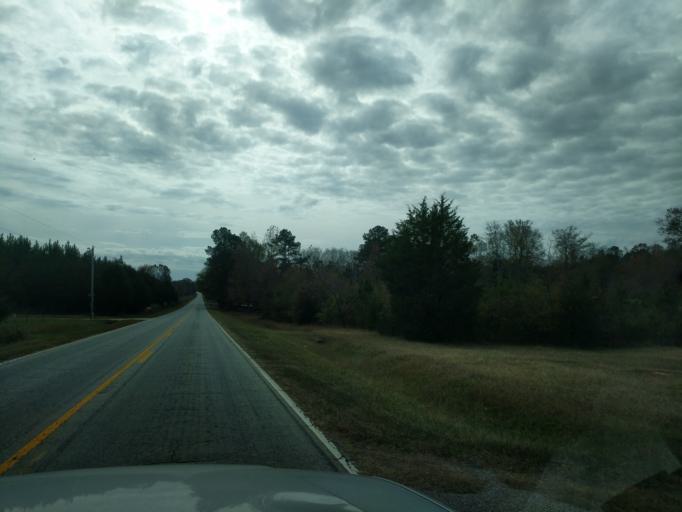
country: US
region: South Carolina
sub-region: Laurens County
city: Joanna
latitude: 34.3459
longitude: -81.8558
